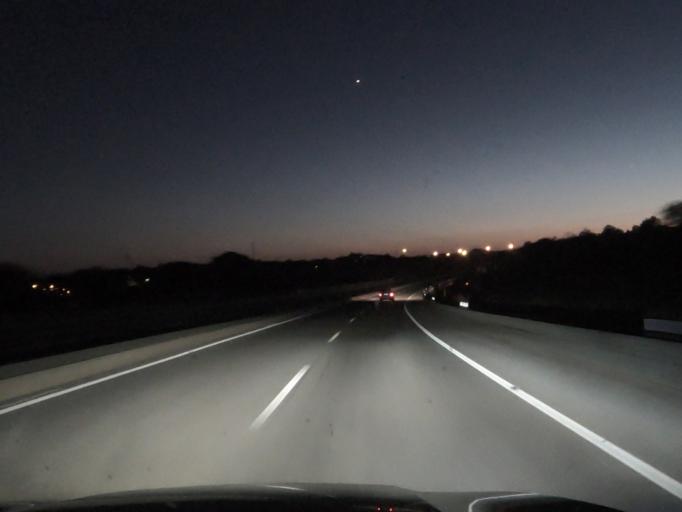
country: PT
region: Faro
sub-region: Loule
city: Loule
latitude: 37.1447
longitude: -8.0316
